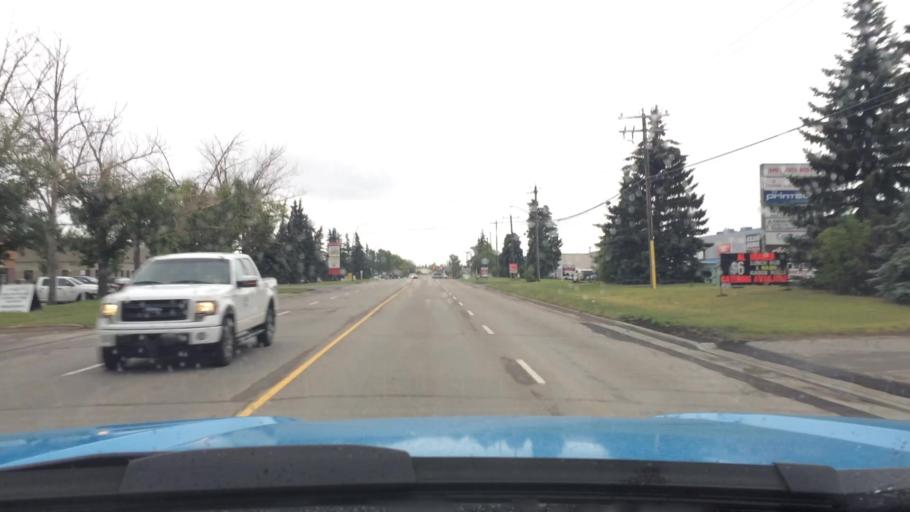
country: CA
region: Alberta
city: Calgary
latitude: 51.0848
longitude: -114.0117
